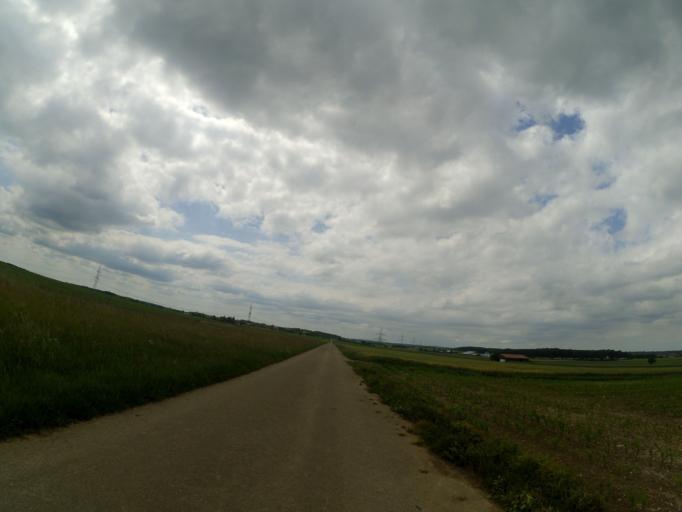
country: DE
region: Baden-Wuerttemberg
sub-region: Tuebingen Region
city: Blaubeuren
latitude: 48.4210
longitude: 9.8259
